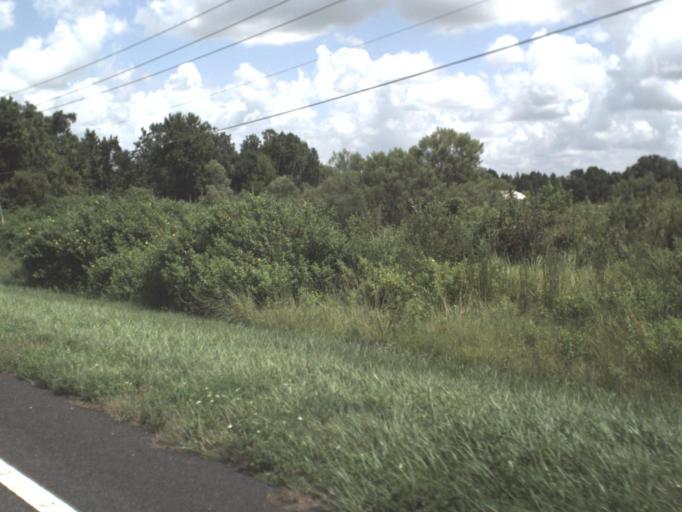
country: US
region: Florida
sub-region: Hardee County
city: Bowling Green
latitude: 27.6149
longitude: -81.8262
